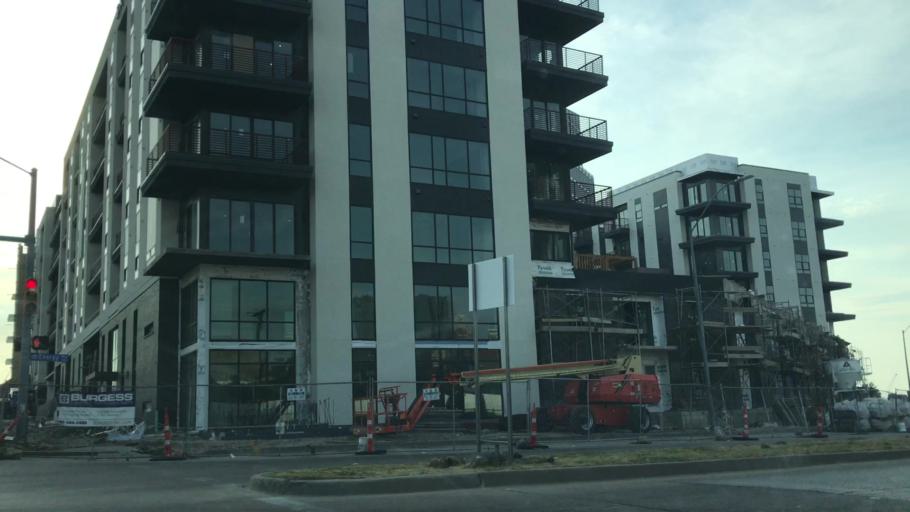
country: US
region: Texas
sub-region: Tarrant County
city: Fort Worth
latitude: 32.7519
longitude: -97.3415
